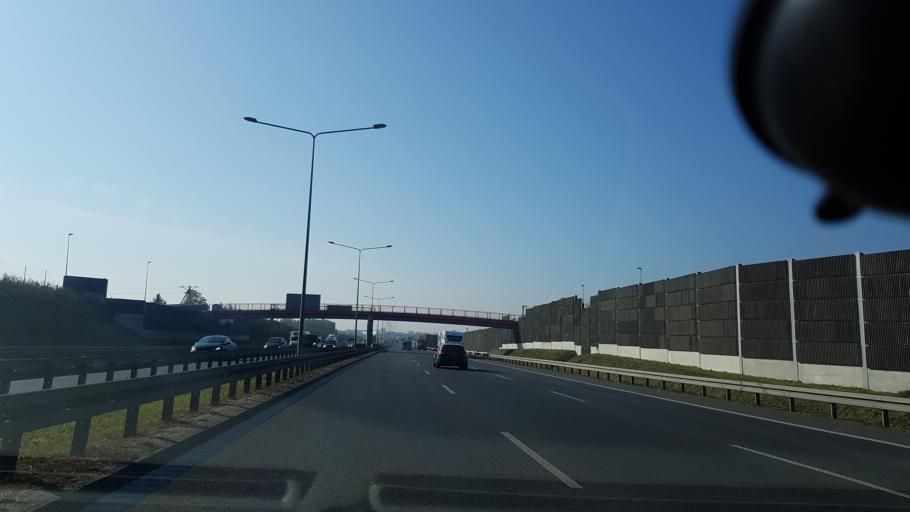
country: PL
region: Masovian Voivodeship
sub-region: Powiat pruszkowski
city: Nowe Grocholice
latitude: 52.1613
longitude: 20.9052
